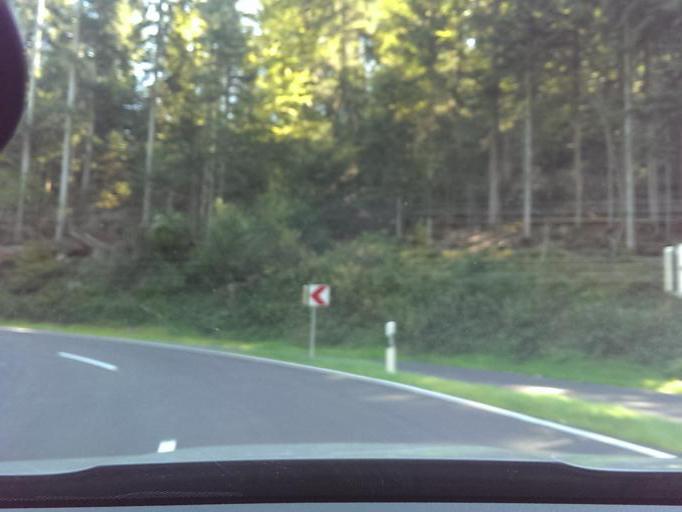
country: DE
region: Baden-Wuerttemberg
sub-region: Karlsruhe Region
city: Bad Herrenalb
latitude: 48.8010
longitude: 8.4636
